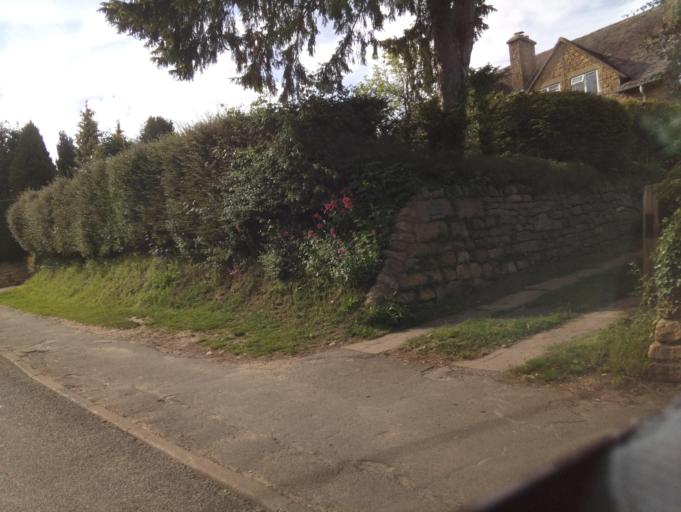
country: GB
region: England
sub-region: Gloucestershire
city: Chipping Campden
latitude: 52.0525
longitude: -1.7700
